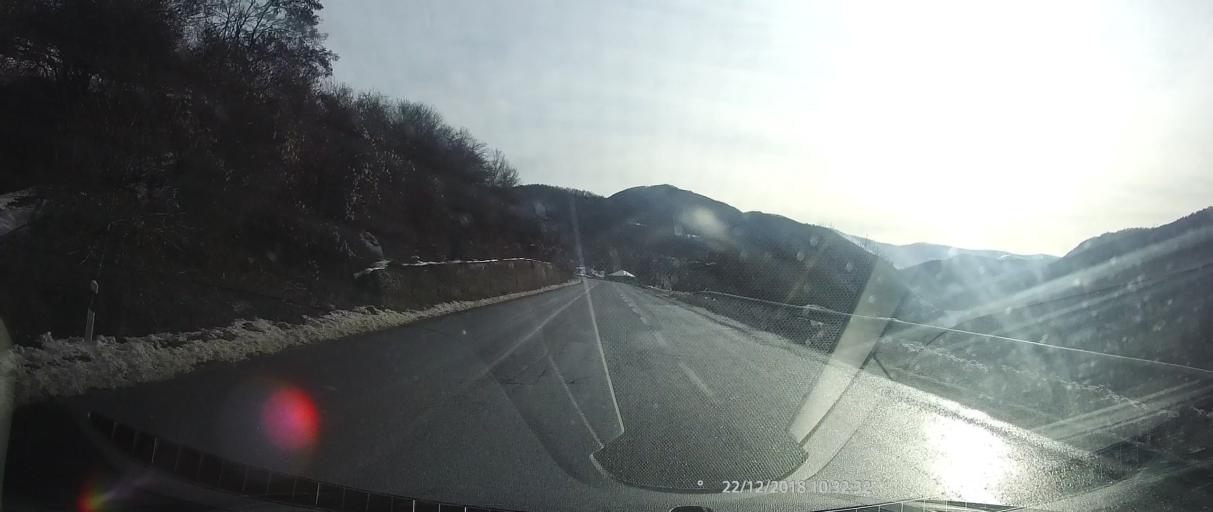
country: MK
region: Kriva Palanka
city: Kriva Palanka
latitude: 42.2189
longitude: 22.4345
